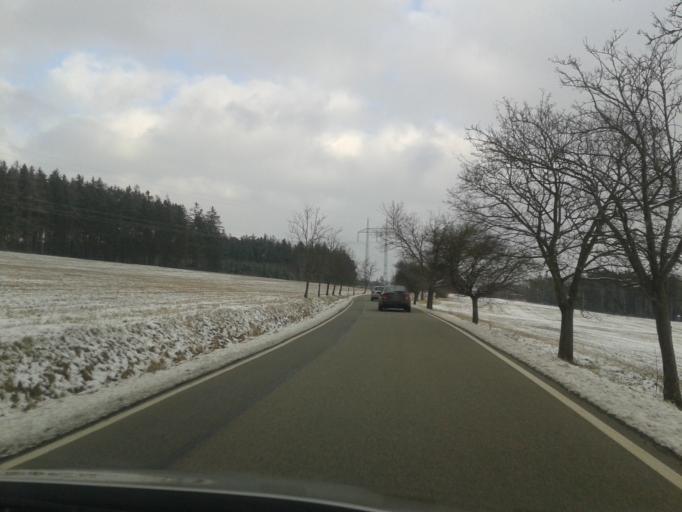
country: CZ
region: Olomoucky
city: Konice
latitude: 49.5884
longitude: 16.8430
